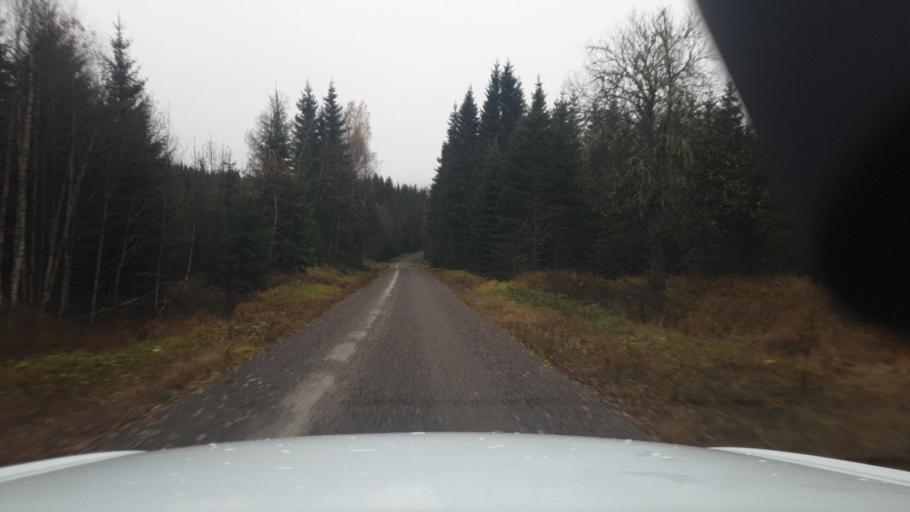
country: SE
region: Vaermland
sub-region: Eda Kommun
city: Charlottenberg
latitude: 60.0271
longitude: 12.6336
